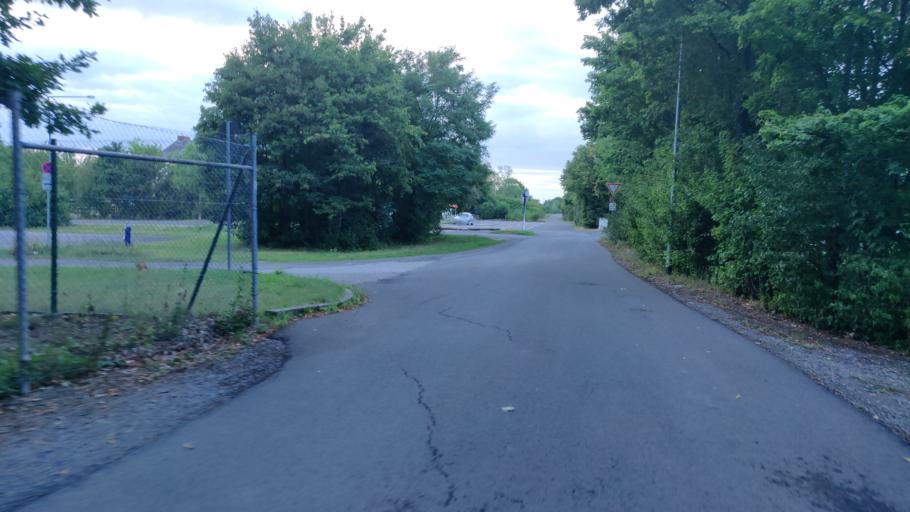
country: DE
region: Bavaria
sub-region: Regierungsbezirk Unterfranken
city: Niederwerrn
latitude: 50.0543
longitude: 10.1979
